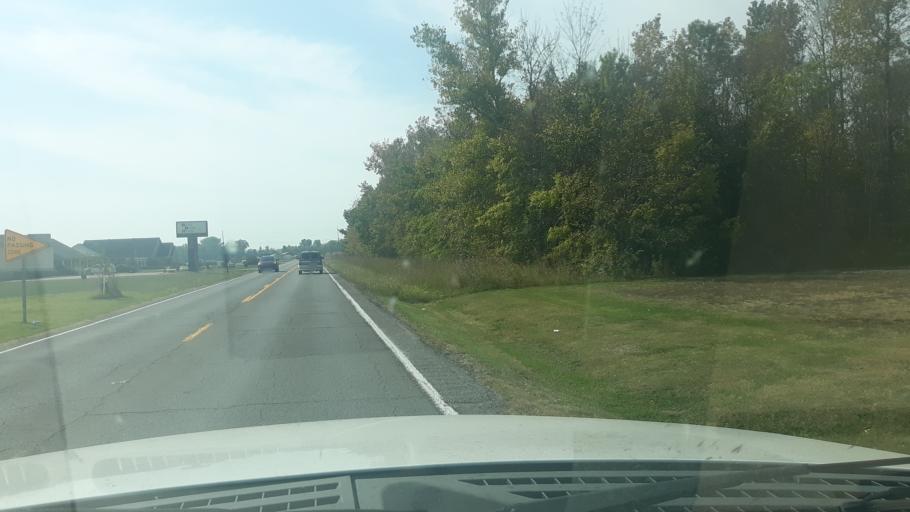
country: US
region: Illinois
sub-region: Saline County
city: Harrisburg
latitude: 37.7244
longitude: -88.5383
